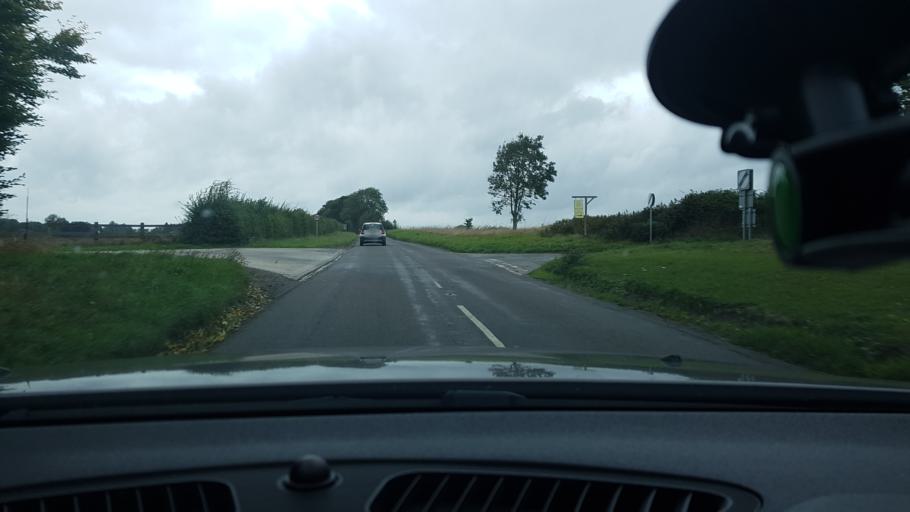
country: GB
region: England
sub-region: Wiltshire
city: Great Bedwyn
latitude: 51.3443
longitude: -1.6158
